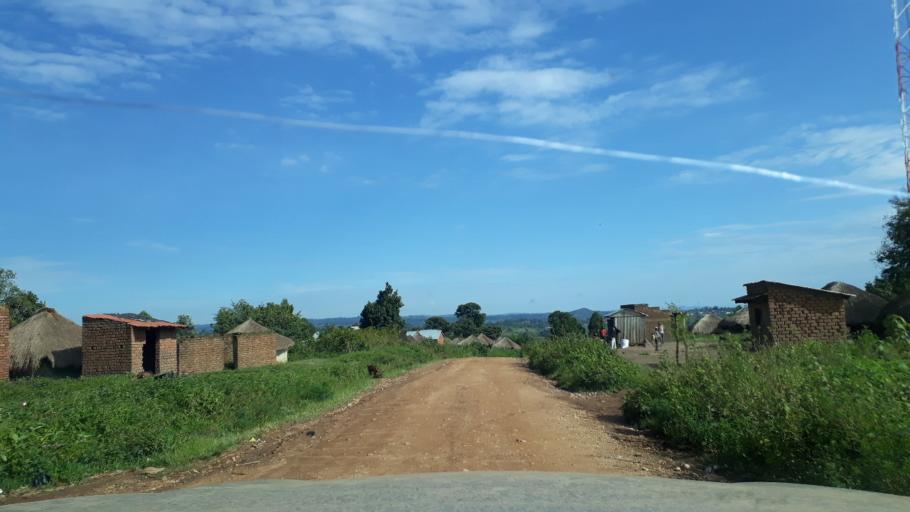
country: UG
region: Northern Region
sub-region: Zombo District
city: Paidha
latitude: 2.3586
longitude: 31.0285
